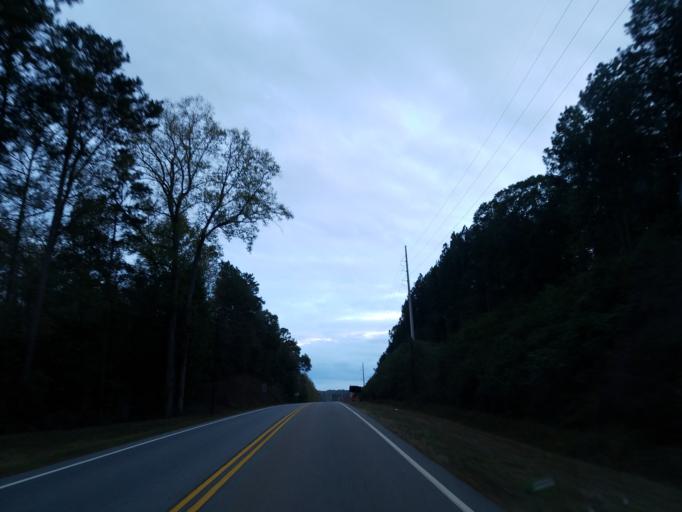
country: US
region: Georgia
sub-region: Dawson County
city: Dawsonville
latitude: 34.3680
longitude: -84.1127
